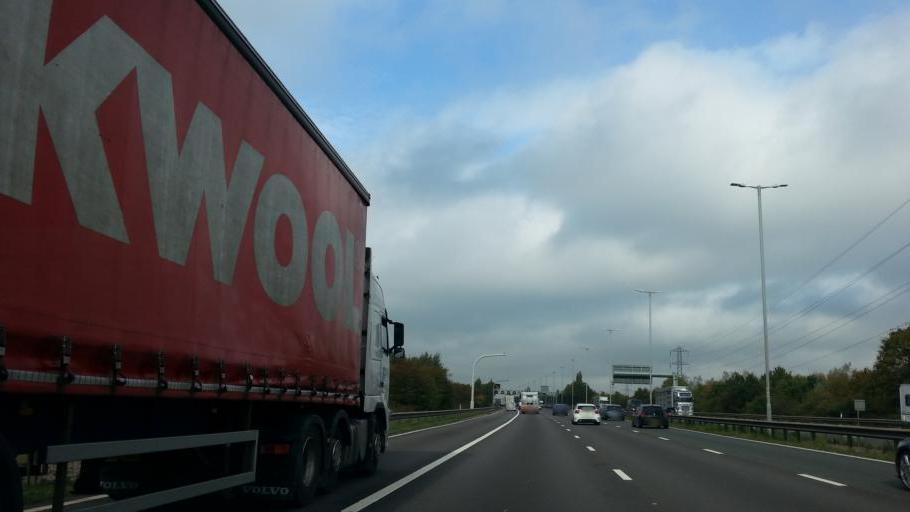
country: GB
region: England
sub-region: Walsall
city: Bloxwich
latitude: 52.6042
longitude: -2.0190
